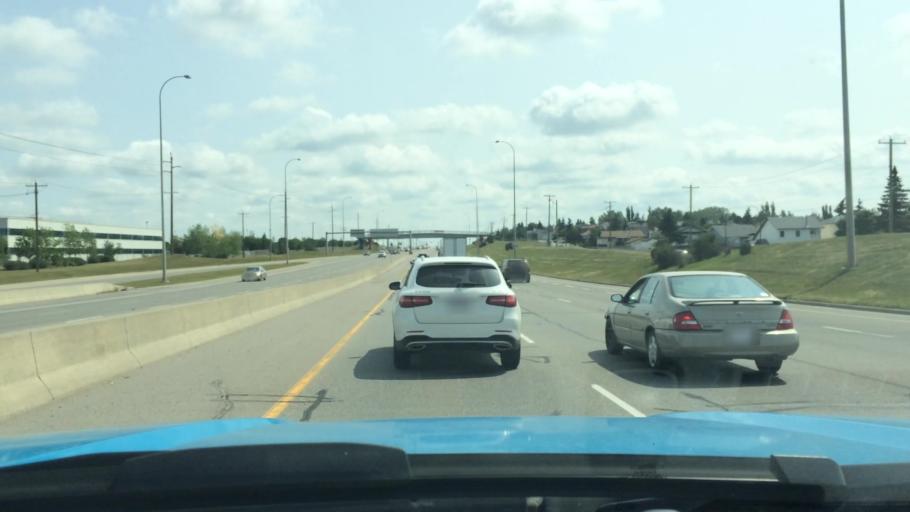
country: CA
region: Alberta
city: Calgary
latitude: 51.0959
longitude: -113.9775
